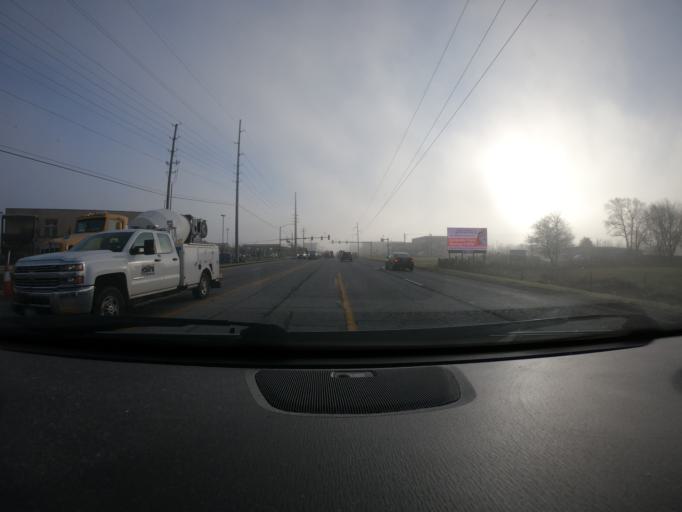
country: US
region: Arkansas
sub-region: Benton County
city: Bentonville
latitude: 36.3572
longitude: -94.2240
